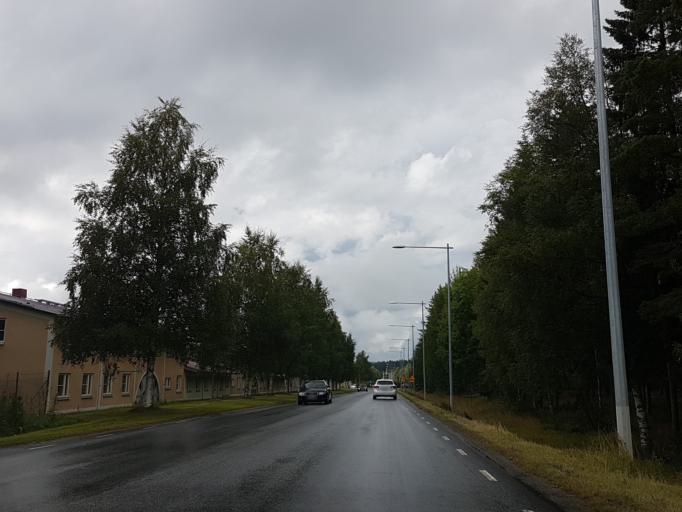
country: SE
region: Vaesterbotten
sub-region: Umea Kommun
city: Ersmark
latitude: 63.8520
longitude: 20.3200
